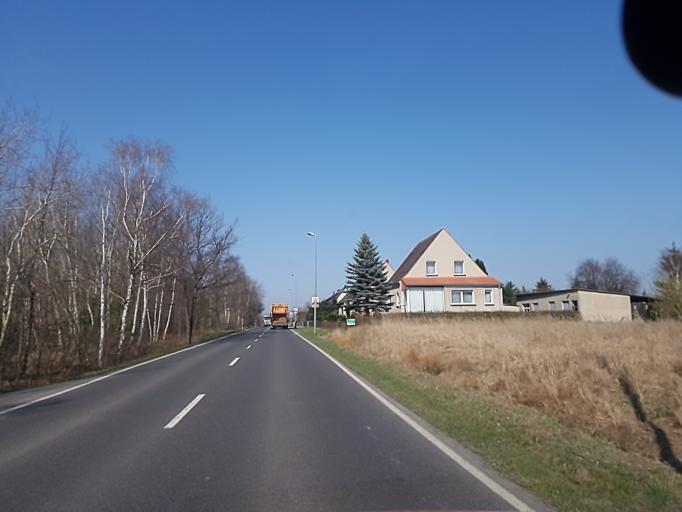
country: DE
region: Brandenburg
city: Forst
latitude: 51.6925
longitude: 14.6033
